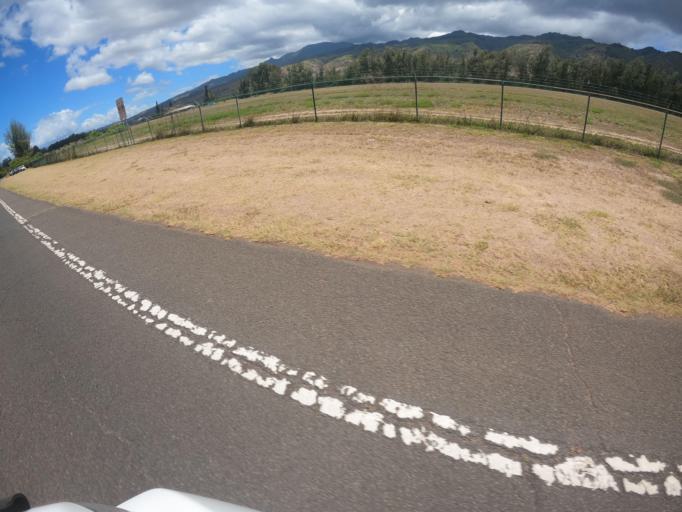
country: US
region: Hawaii
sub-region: Honolulu County
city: Mokuleia
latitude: 21.5814
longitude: -158.1872
